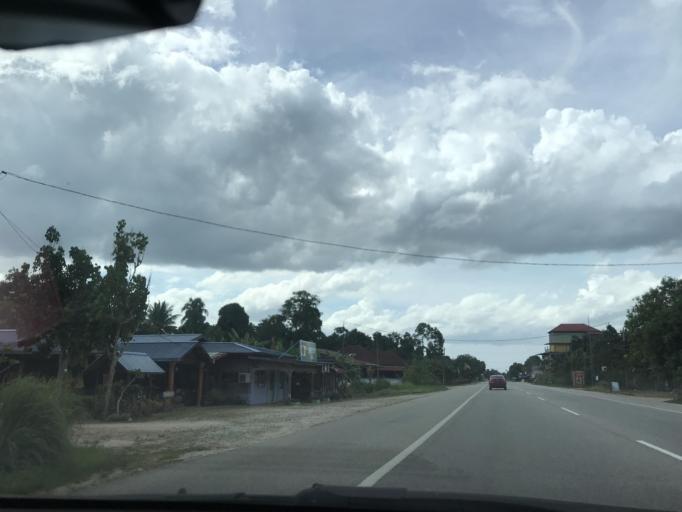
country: MY
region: Kelantan
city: Kampong Pangkal Kalong
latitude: 5.9227
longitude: 102.1895
